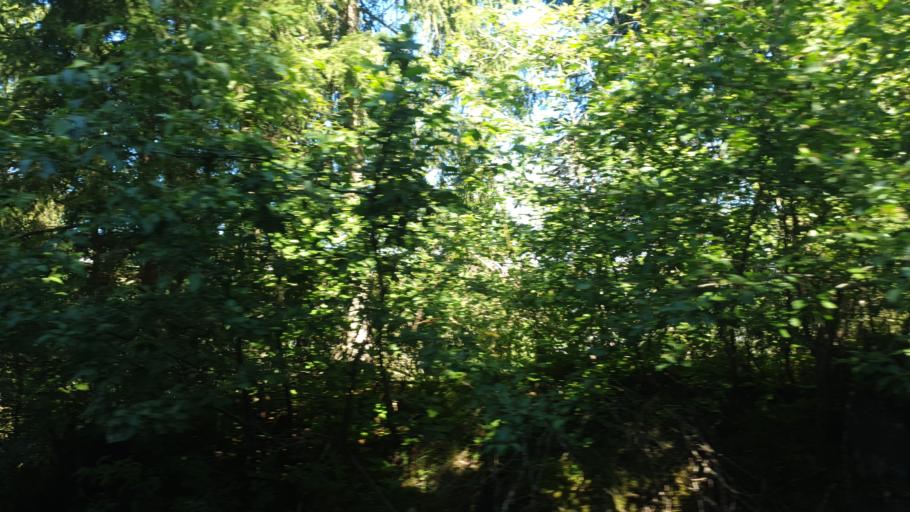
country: NO
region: Sor-Trondelag
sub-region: Meldal
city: Meldal
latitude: 63.1662
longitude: 9.7378
